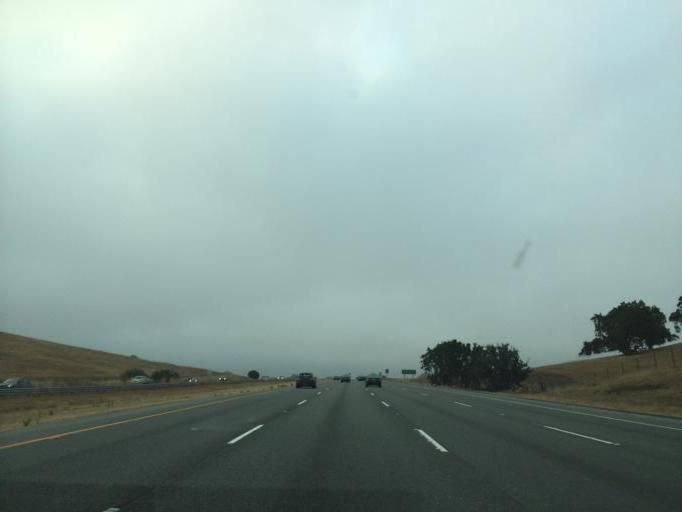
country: US
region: California
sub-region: San Mateo County
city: Ladera
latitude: 37.3990
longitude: -122.1819
